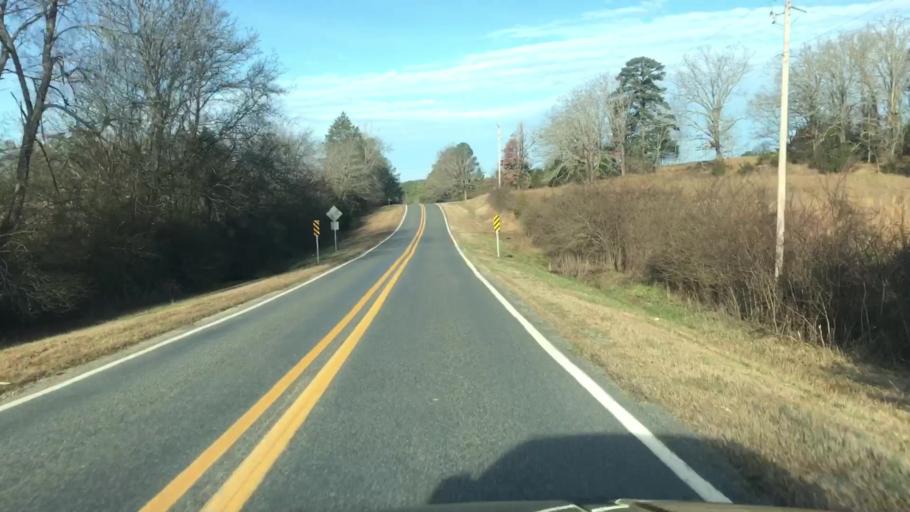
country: US
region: Arkansas
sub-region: Garland County
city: Rockwell
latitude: 34.4768
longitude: -93.2646
